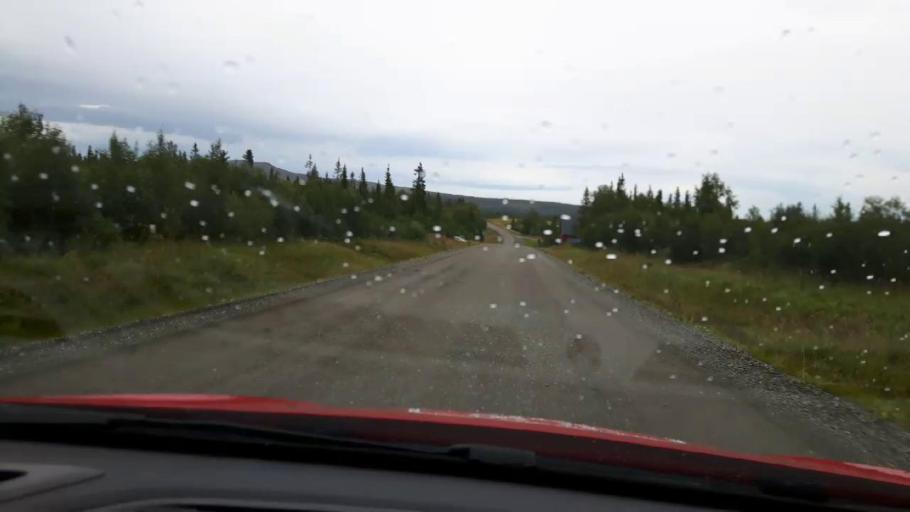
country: NO
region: Nord-Trondelag
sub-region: Meraker
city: Meraker
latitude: 63.5577
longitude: 12.3357
